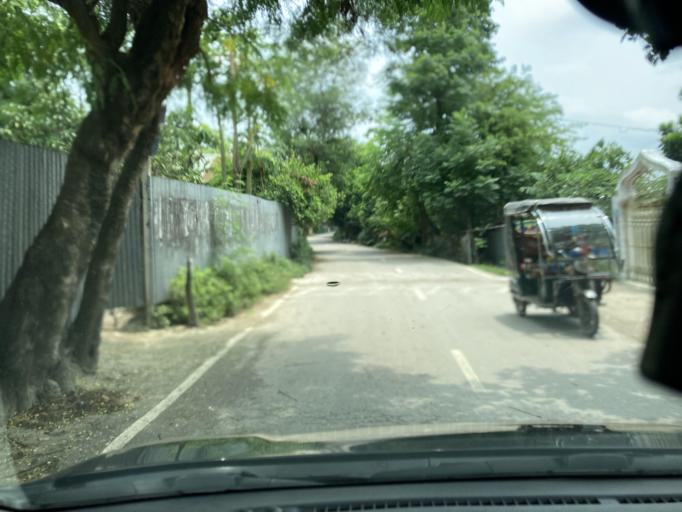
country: BD
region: Dhaka
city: Dohar
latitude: 23.7661
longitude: 90.1949
